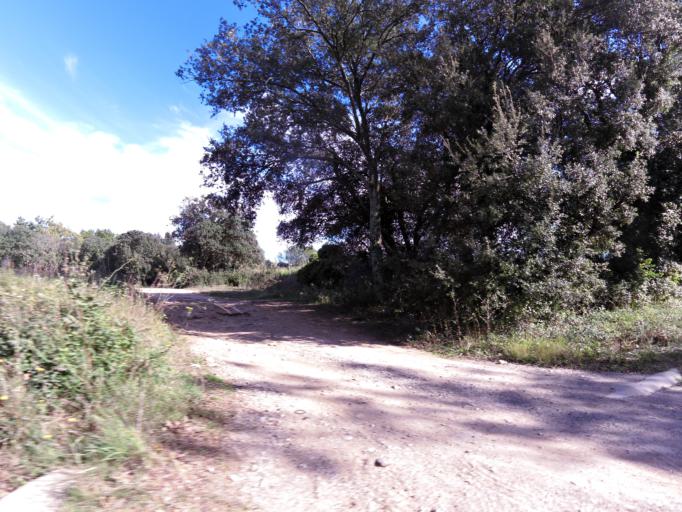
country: FR
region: Languedoc-Roussillon
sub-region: Departement du Gard
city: Villevieille
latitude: 43.7988
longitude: 4.1191
